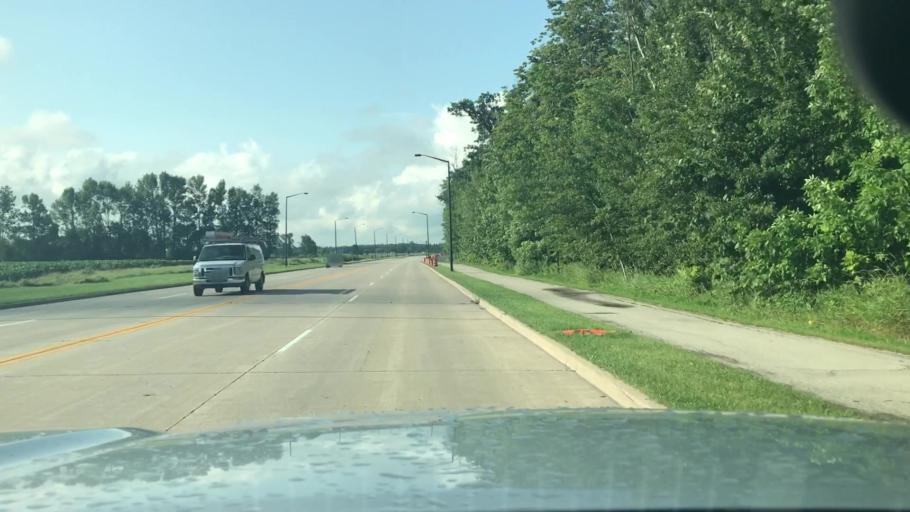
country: US
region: Wisconsin
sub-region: Brown County
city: Bellevue
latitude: 44.4751
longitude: -87.9172
